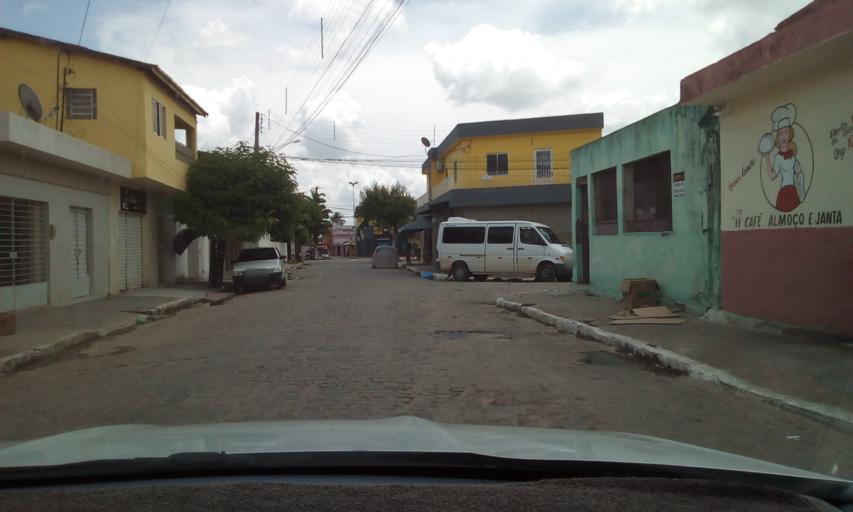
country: BR
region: Pernambuco
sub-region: Bonito
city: Bonito
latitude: -8.4716
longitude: -35.7284
